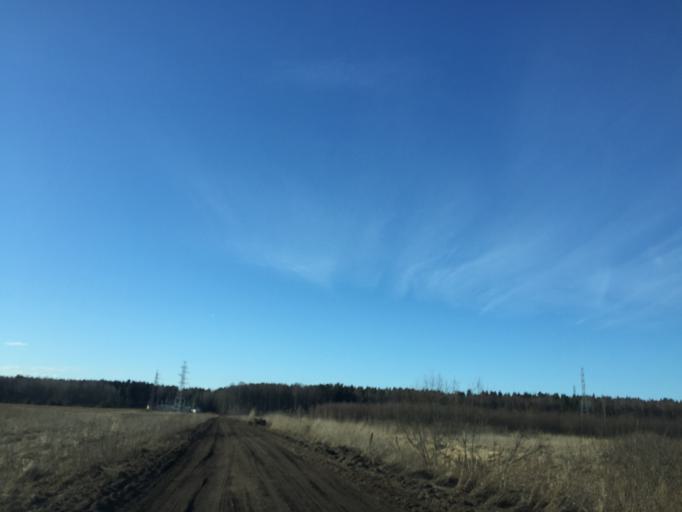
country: LV
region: Babite
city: Pinki
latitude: 56.9635
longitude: 23.8918
